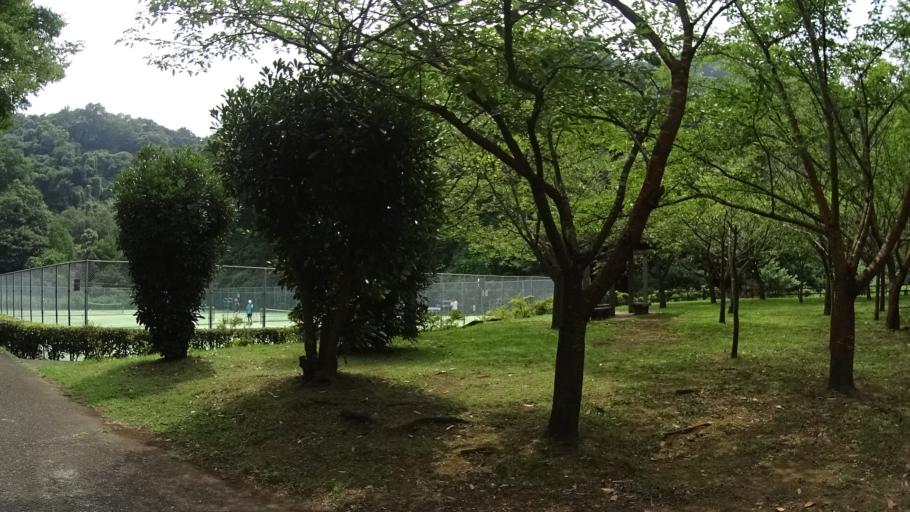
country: JP
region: Kanagawa
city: Zushi
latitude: 35.2850
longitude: 139.6038
